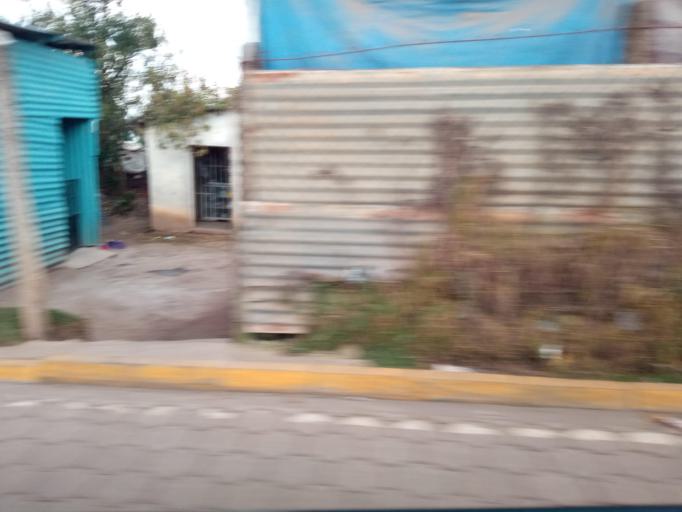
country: GT
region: Quetzaltenango
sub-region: Municipio de La Esperanza
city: La Esperanza
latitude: 14.8545
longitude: -91.5527
